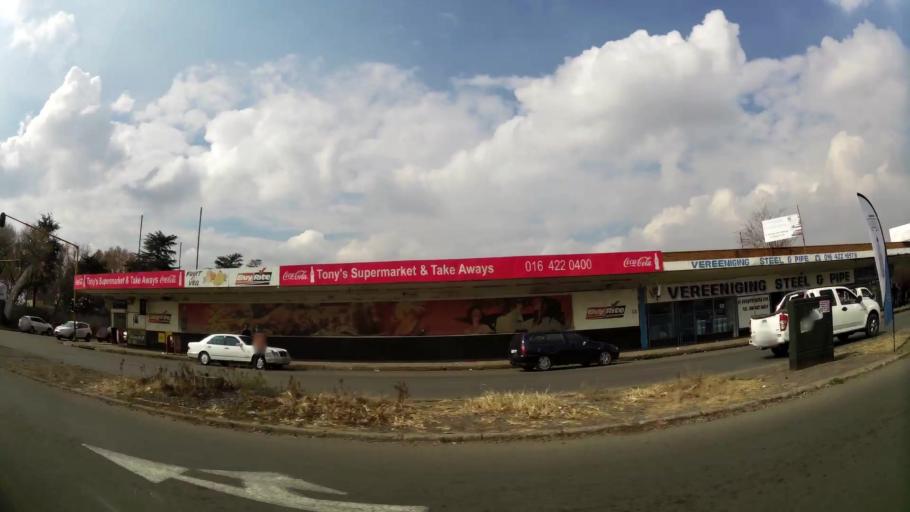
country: ZA
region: Gauteng
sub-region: Sedibeng District Municipality
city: Vereeniging
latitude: -26.6807
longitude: 27.9301
